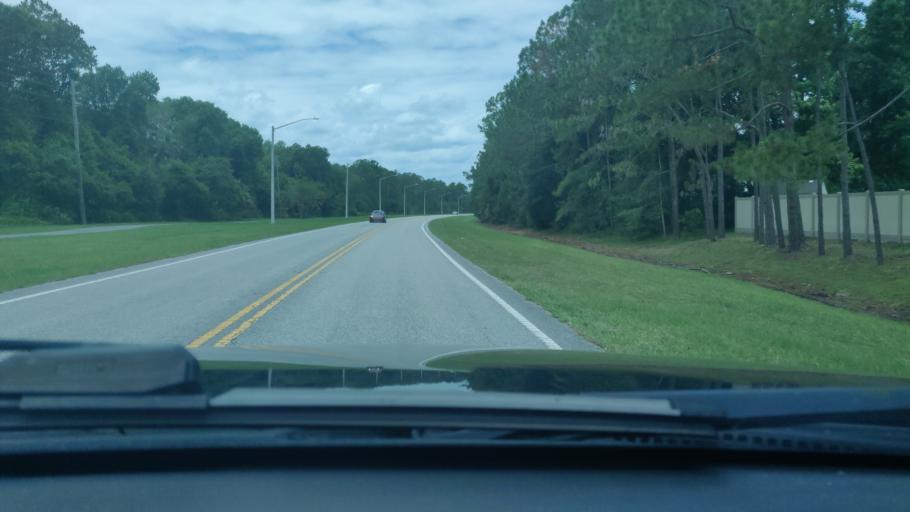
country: US
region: Florida
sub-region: Flagler County
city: Bunnell
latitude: 29.5277
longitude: -81.2476
